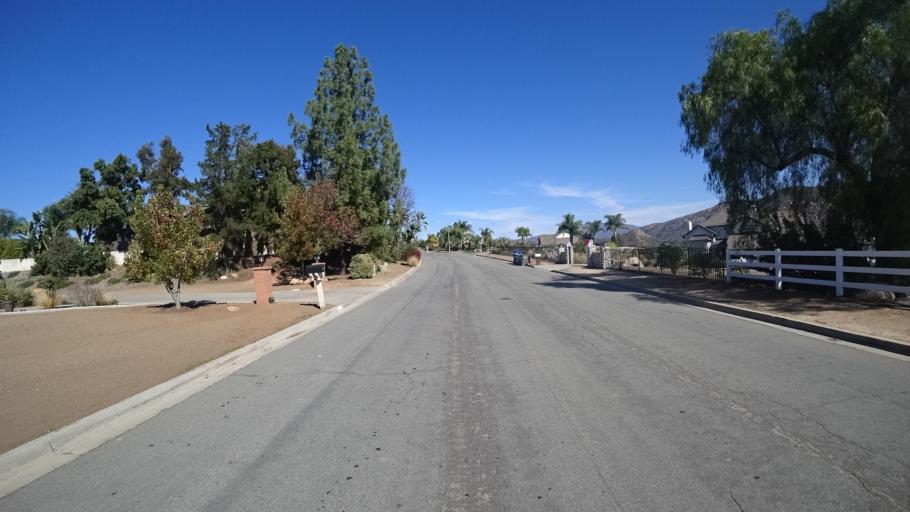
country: US
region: California
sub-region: San Diego County
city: Crest
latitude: 32.8573
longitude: -116.8716
